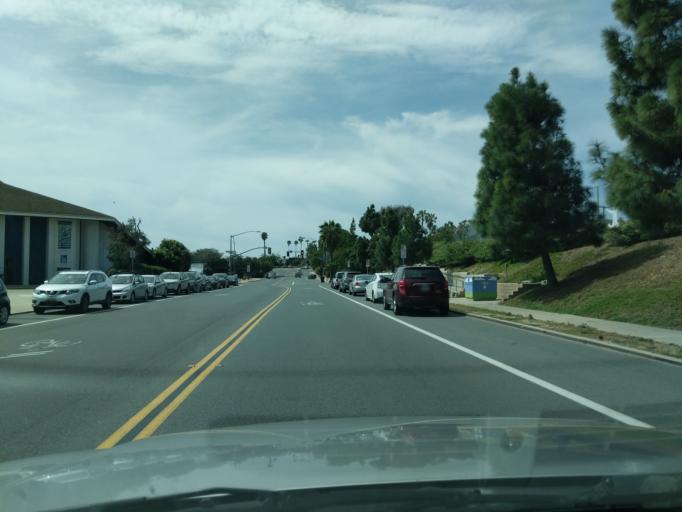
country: US
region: California
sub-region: San Diego County
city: Coronado
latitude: 32.7318
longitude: -117.2427
